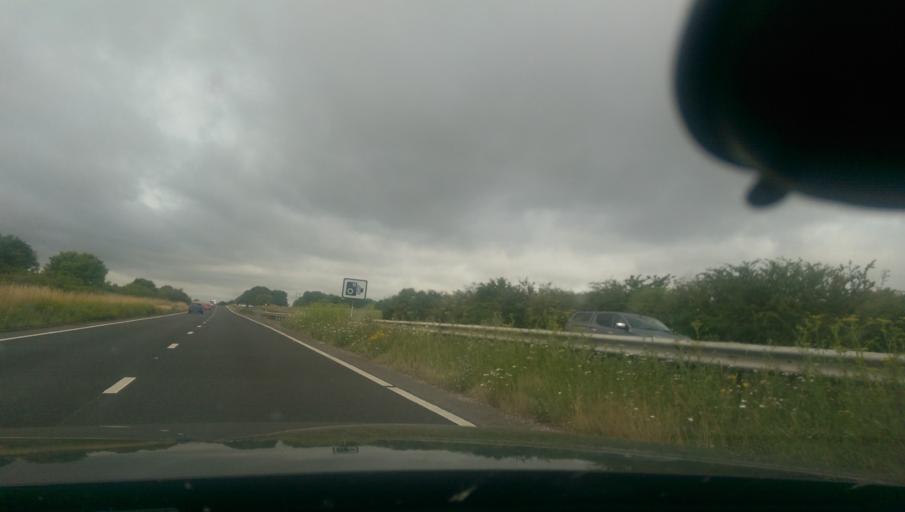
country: GB
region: England
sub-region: Wiltshire
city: Allington
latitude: 51.1809
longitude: -1.7226
